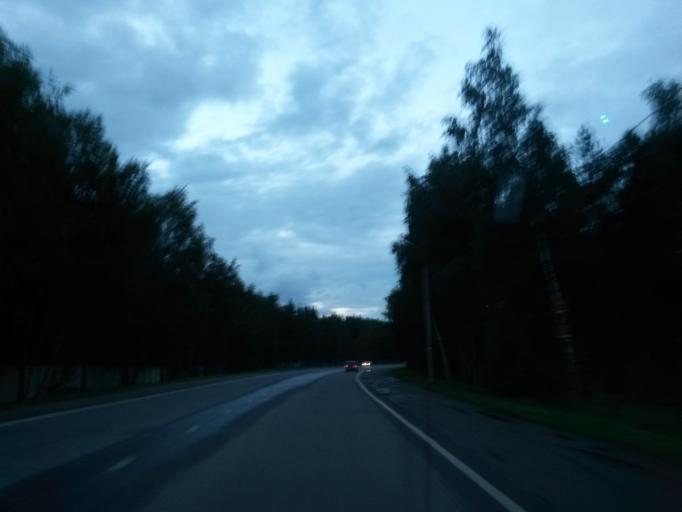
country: RU
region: Jaroslavl
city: Yaroslavl
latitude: 57.6751
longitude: 39.9061
